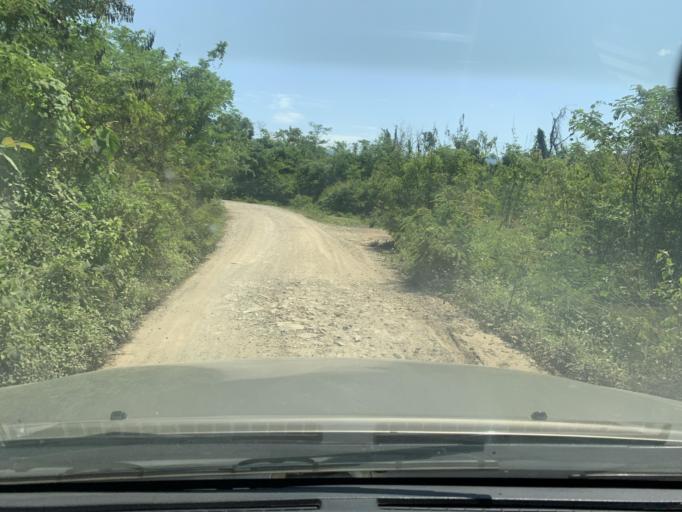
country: LA
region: Louangphabang
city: Louangphabang
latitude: 19.8981
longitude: 102.2144
